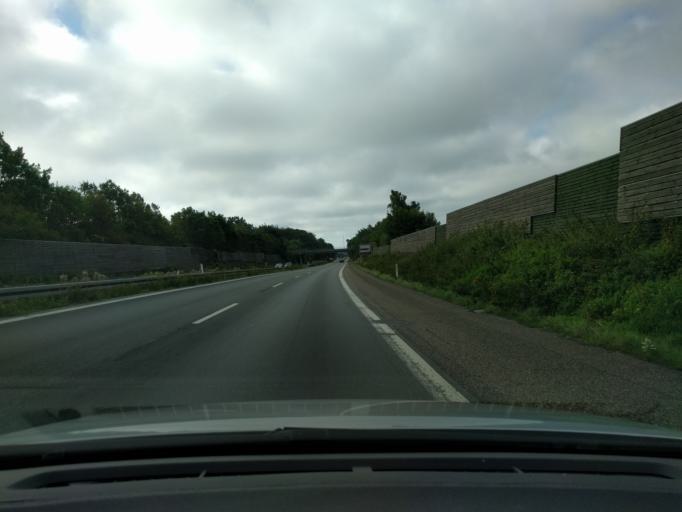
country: DK
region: South Denmark
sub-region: Nyborg Kommune
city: Nyborg
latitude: 55.3257
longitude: 10.8042
